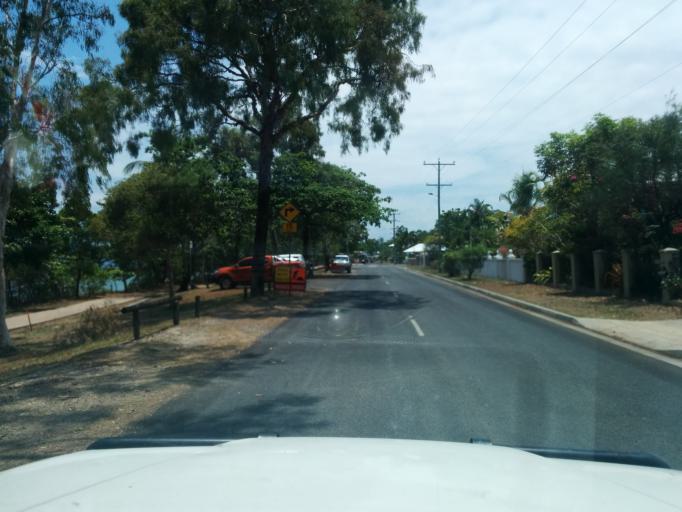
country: AU
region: Queensland
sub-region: Cairns
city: Yorkeys Knob
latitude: -16.8355
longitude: 145.7383
